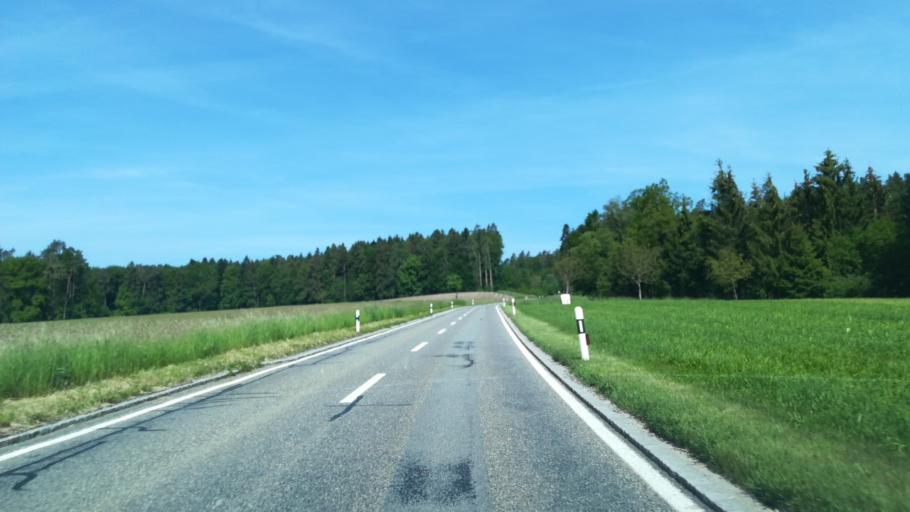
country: CH
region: Thurgau
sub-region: Frauenfeld District
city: Pfyn
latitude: 47.6047
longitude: 8.9426
